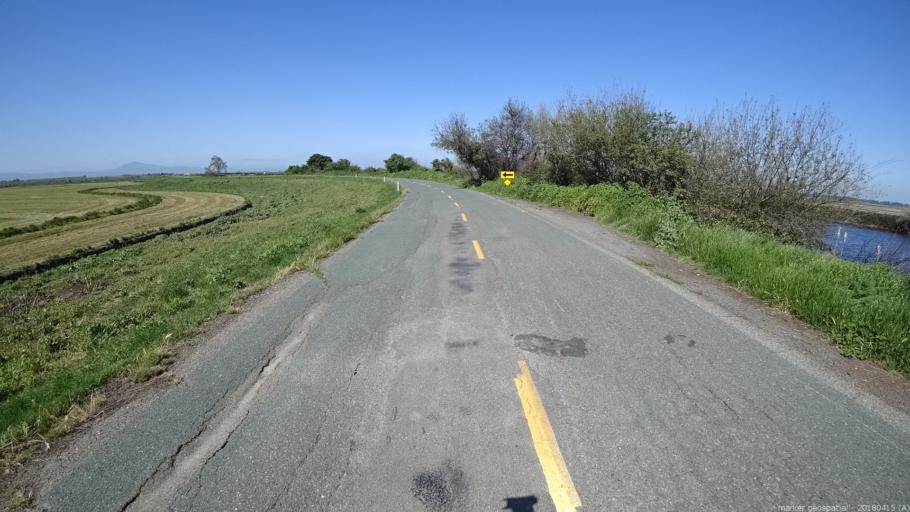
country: US
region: California
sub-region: Solano County
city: Rio Vista
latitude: 38.1182
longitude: -121.6484
